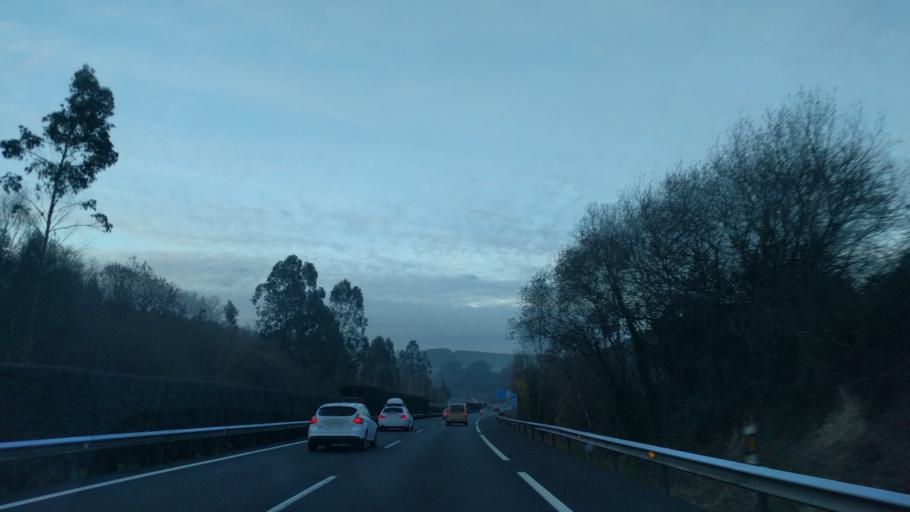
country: ES
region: Cantabria
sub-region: Provincia de Cantabria
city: Colindres
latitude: 43.3935
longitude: -3.4810
